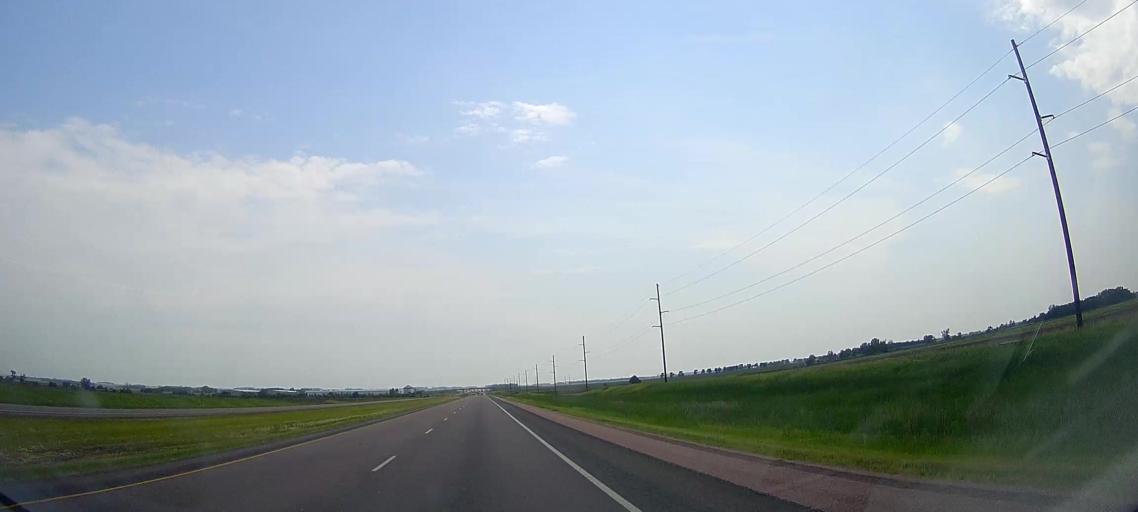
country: US
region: South Dakota
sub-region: Union County
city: Beresford
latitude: 43.2254
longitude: -96.7963
